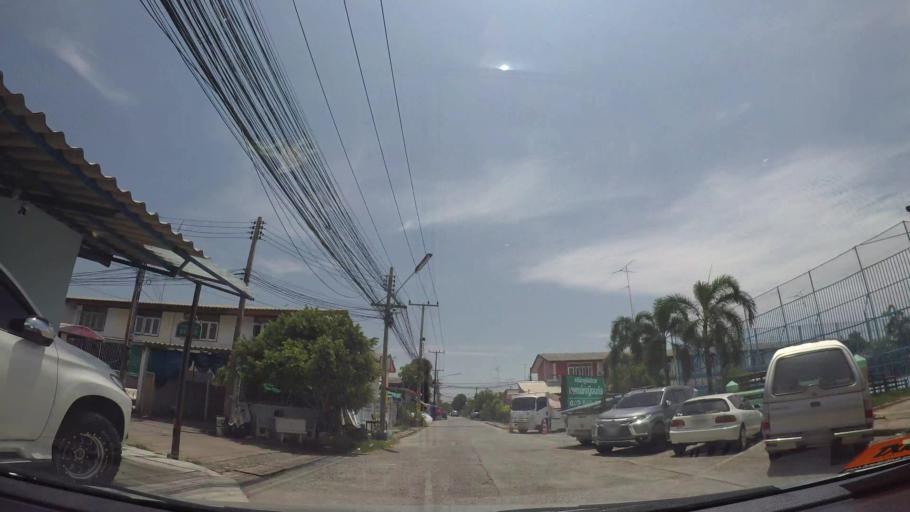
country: TH
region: Chon Buri
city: Chon Buri
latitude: 13.3287
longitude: 100.9416
